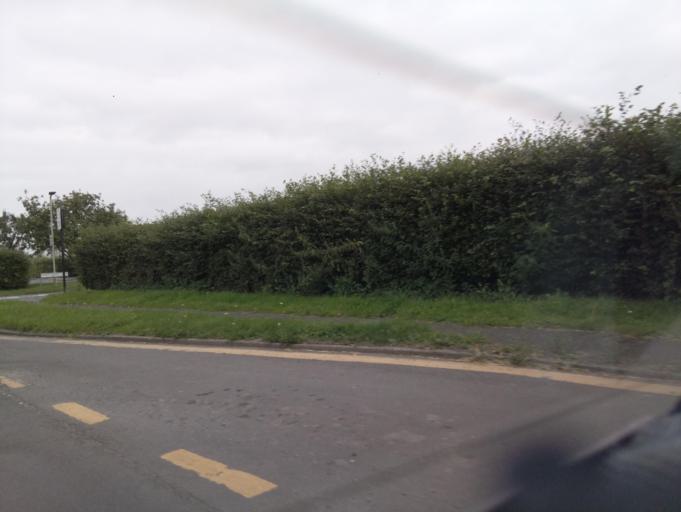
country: GB
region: England
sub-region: Shropshire
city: Shawbury
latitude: 52.7863
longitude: -2.6606
